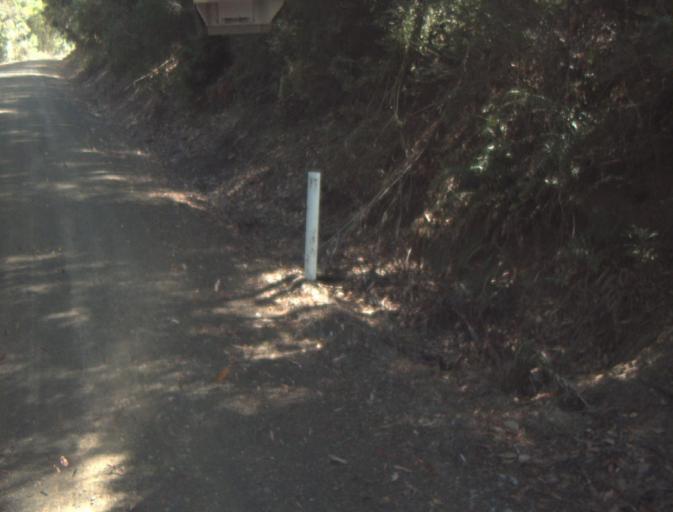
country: AU
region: Tasmania
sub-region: Dorset
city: Scottsdale
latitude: -41.2837
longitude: 147.3391
